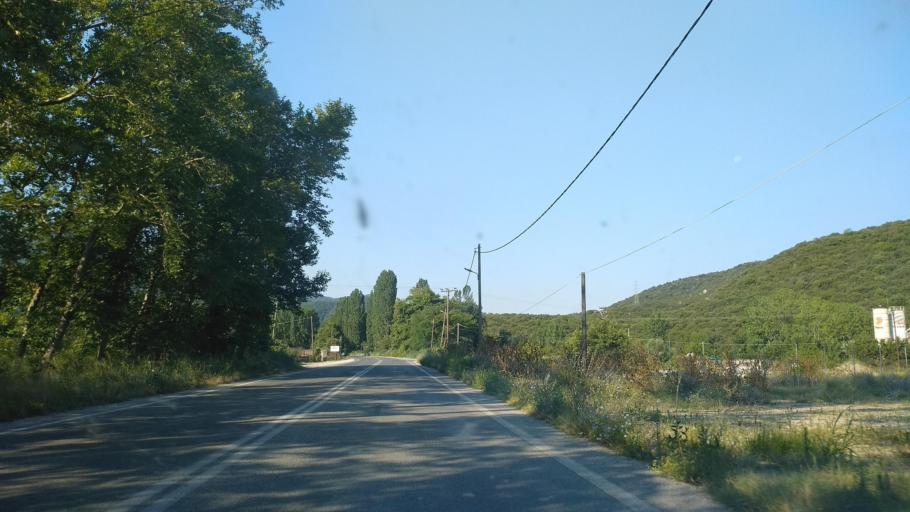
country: GR
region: Central Macedonia
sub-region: Nomos Thessalonikis
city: Stavros
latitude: 40.6814
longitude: 23.6746
